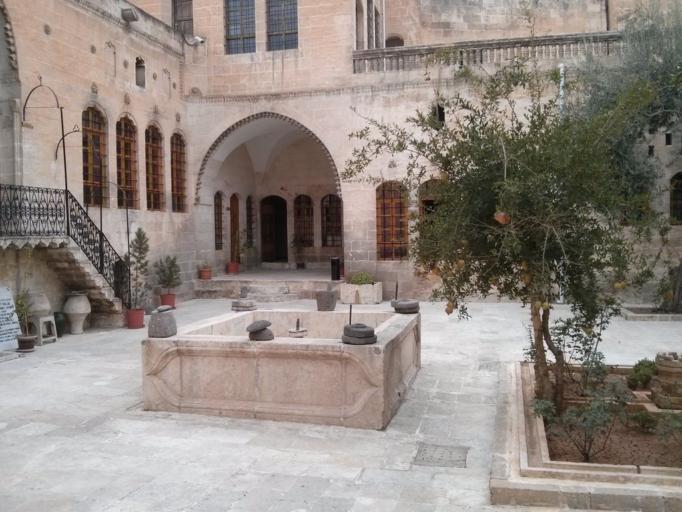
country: TR
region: Sanliurfa
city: Sanliurfa
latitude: 37.1537
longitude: 38.7903
